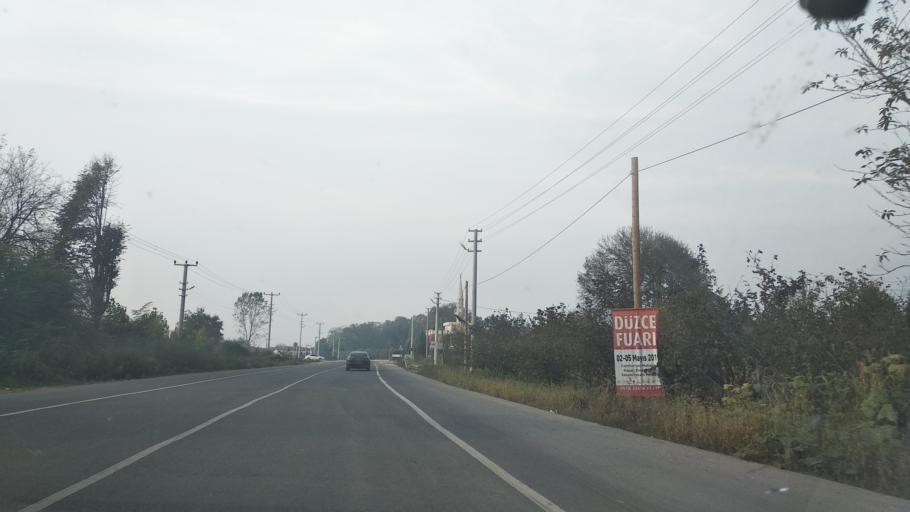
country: TR
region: Duzce
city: Duzce
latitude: 40.8239
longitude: 31.1756
